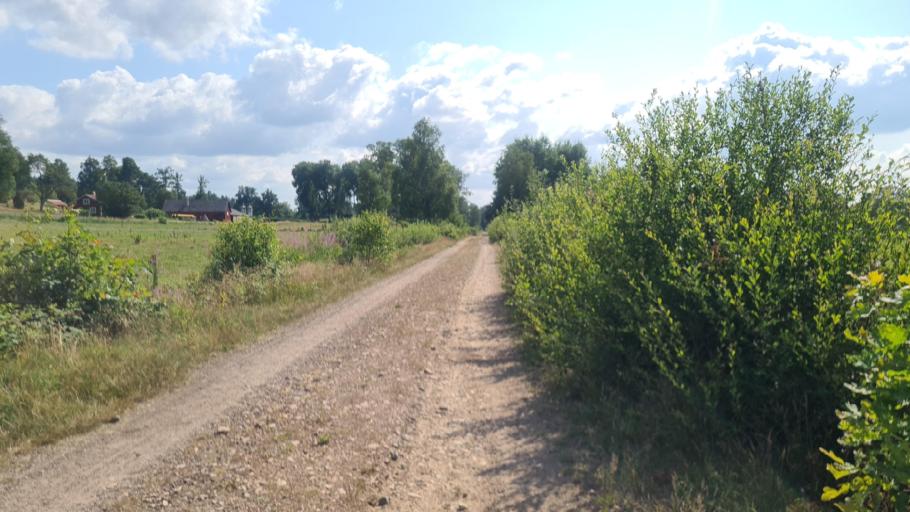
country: SE
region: Kronoberg
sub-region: Ljungby Kommun
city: Ljungby
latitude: 56.7744
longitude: 13.9007
